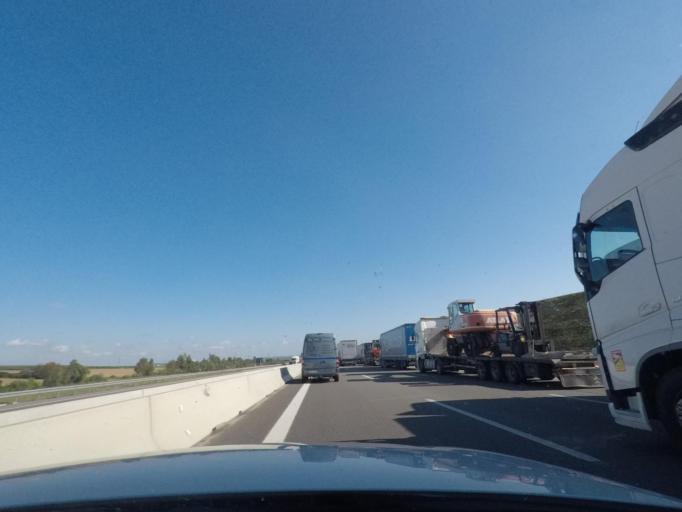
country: DE
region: Baden-Wuerttemberg
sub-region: Regierungsbezirk Stuttgart
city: Bad Rappenau
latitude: 49.1931
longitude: 9.1086
